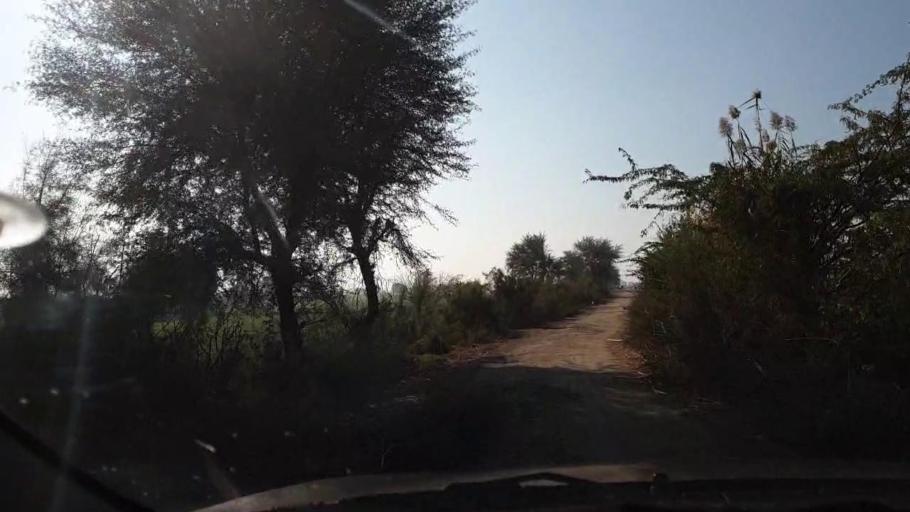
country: PK
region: Sindh
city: Sinjhoro
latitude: 26.0232
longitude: 68.8056
